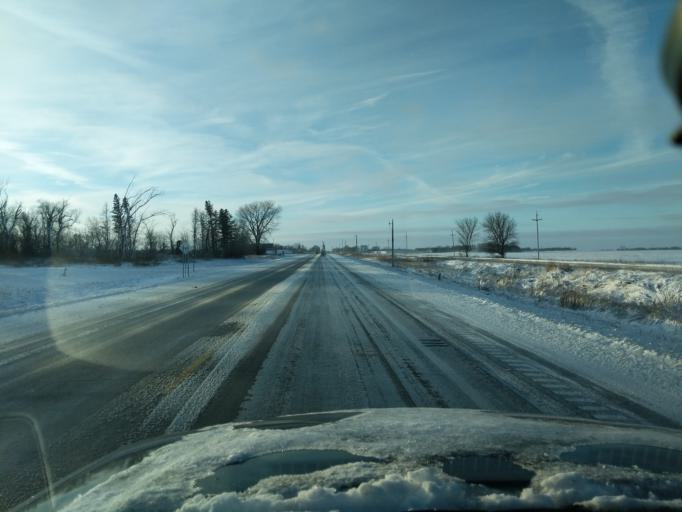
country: US
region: Minnesota
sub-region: Renville County
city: Olivia
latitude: 44.7746
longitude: -94.9582
